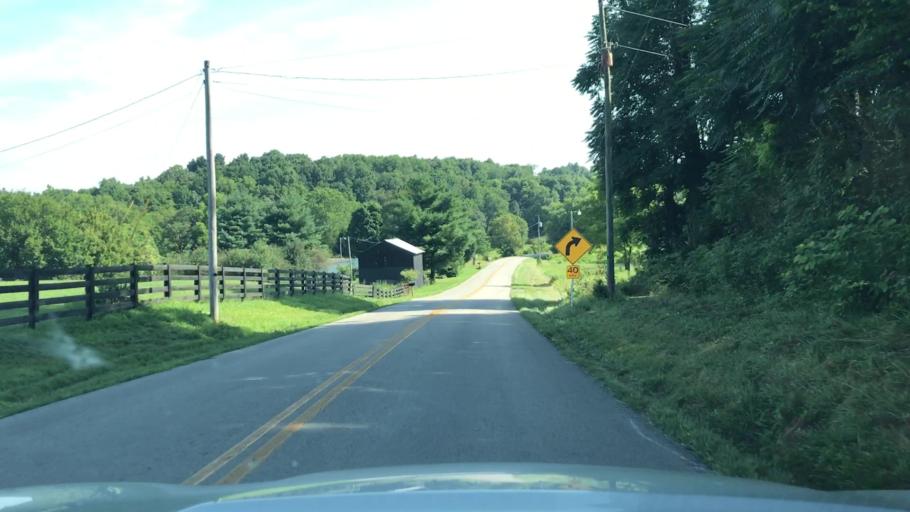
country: US
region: Kentucky
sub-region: Clinton County
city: Albany
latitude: 36.7413
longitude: -85.0125
